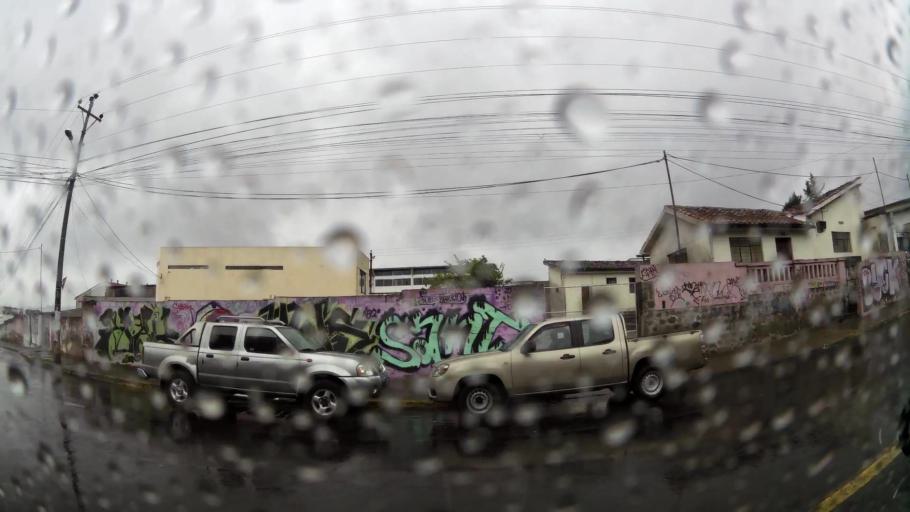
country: EC
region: Pichincha
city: Quito
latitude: -0.1095
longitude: -78.4963
